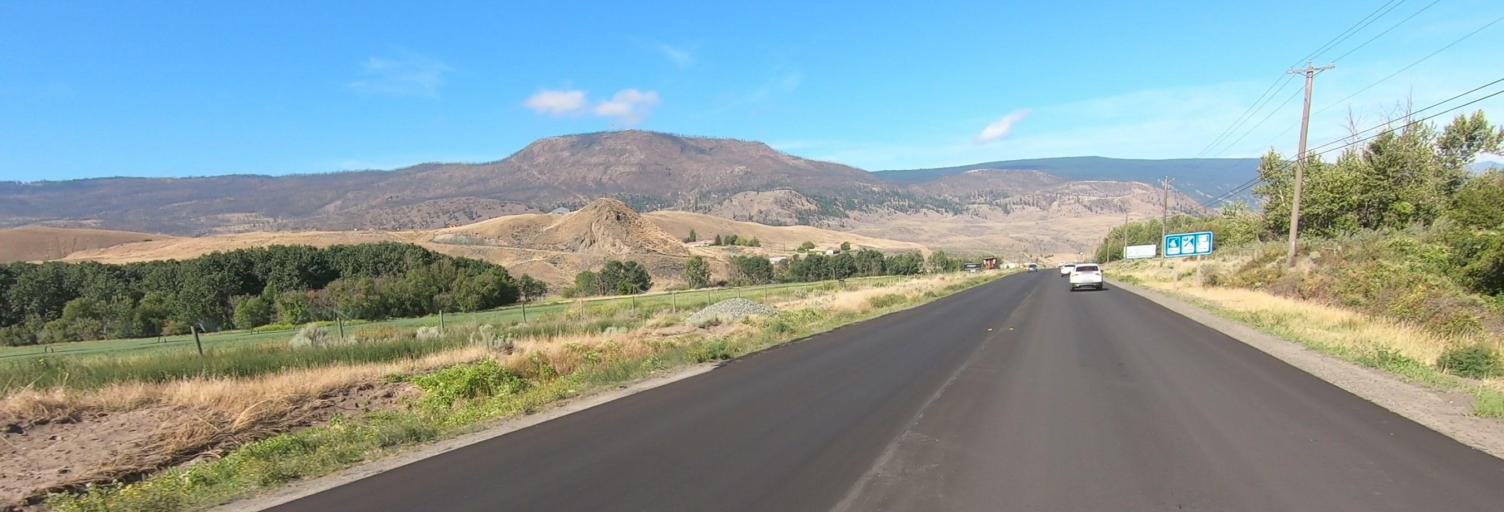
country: CA
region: British Columbia
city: Cache Creek
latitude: 50.8080
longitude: -121.2988
